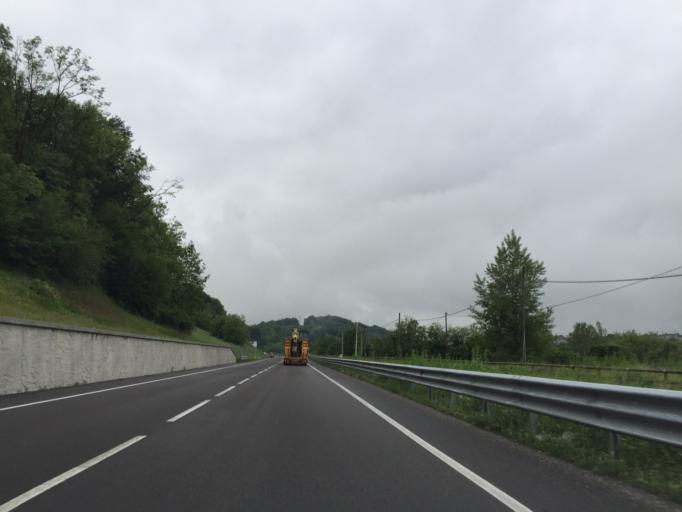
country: IT
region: Veneto
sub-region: Provincia di Belluno
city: Castion
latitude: 46.1397
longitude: 12.2349
